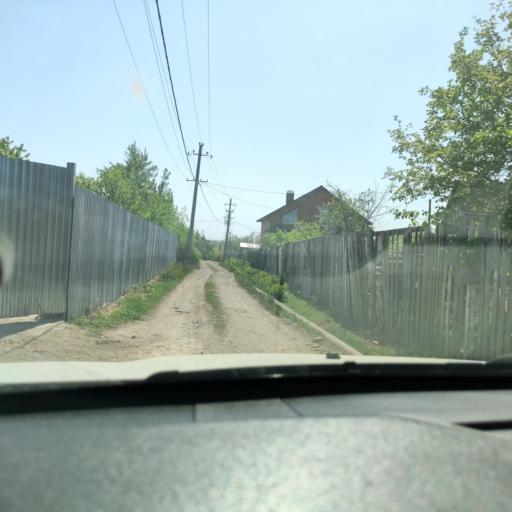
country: RU
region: Samara
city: Petra-Dubrava
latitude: 53.2756
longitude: 50.3286
